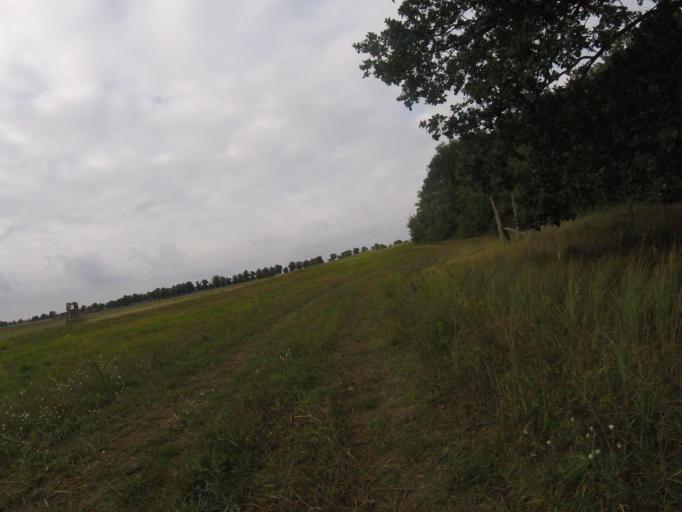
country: DE
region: Brandenburg
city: Mittenwalde
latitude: 52.2660
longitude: 13.4991
